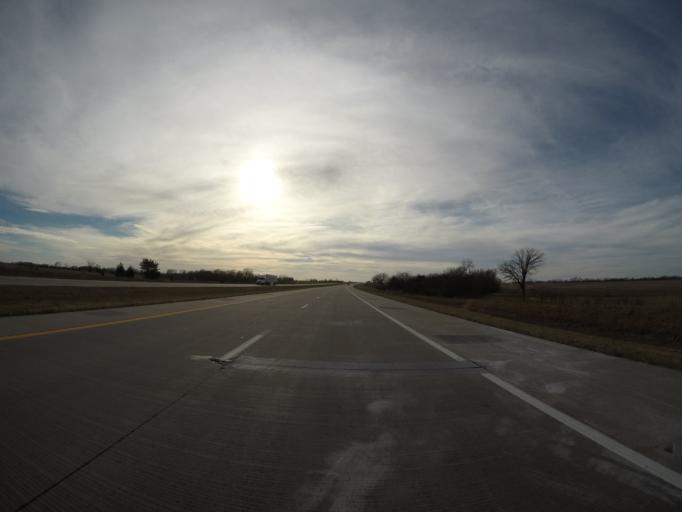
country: US
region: Kansas
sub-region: Franklin County
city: Wellsville
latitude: 38.6811
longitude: -95.1282
